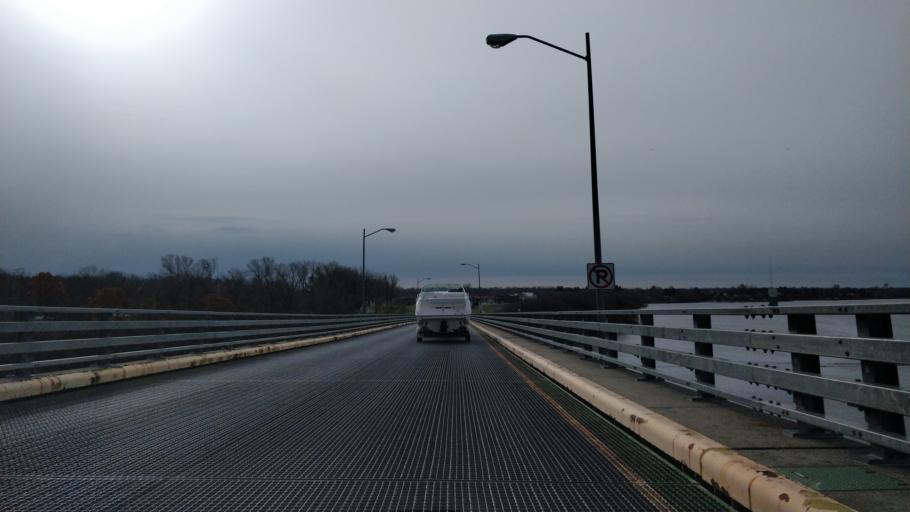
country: US
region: New York
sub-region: St. Lawrence County
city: Ogdensburg
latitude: 44.7295
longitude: -75.4557
